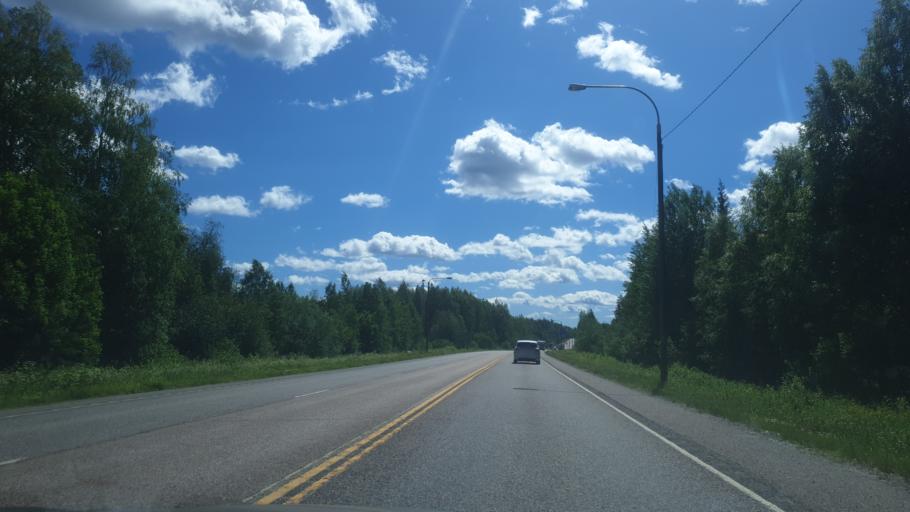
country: FI
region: Northern Savo
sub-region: Varkaus
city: Varkaus
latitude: 62.3556
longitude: 27.8142
